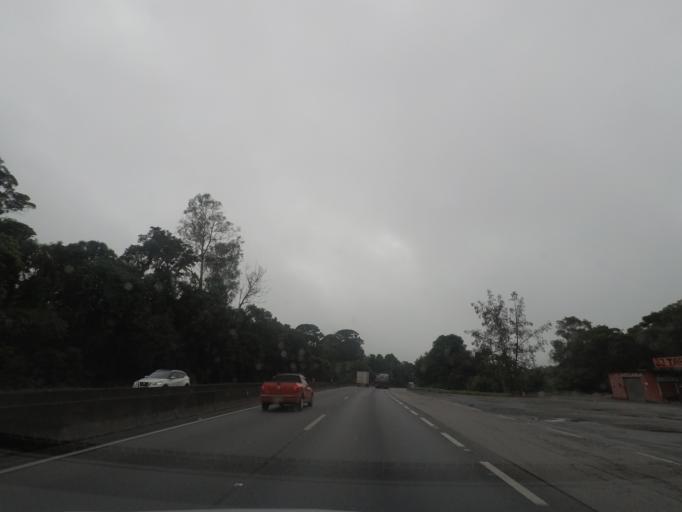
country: BR
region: Parana
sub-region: Campina Grande Do Sul
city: Campina Grande do Sul
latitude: -25.3071
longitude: -48.9975
